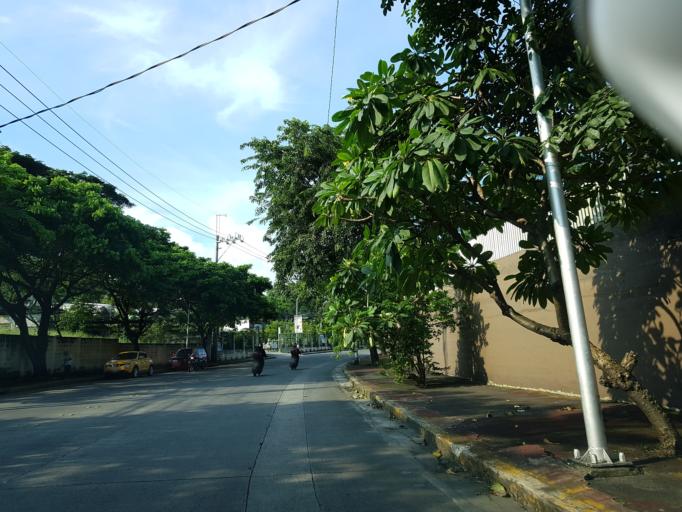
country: PH
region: Metro Manila
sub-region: Pasig
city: Pasig City
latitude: 14.5996
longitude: 121.0710
